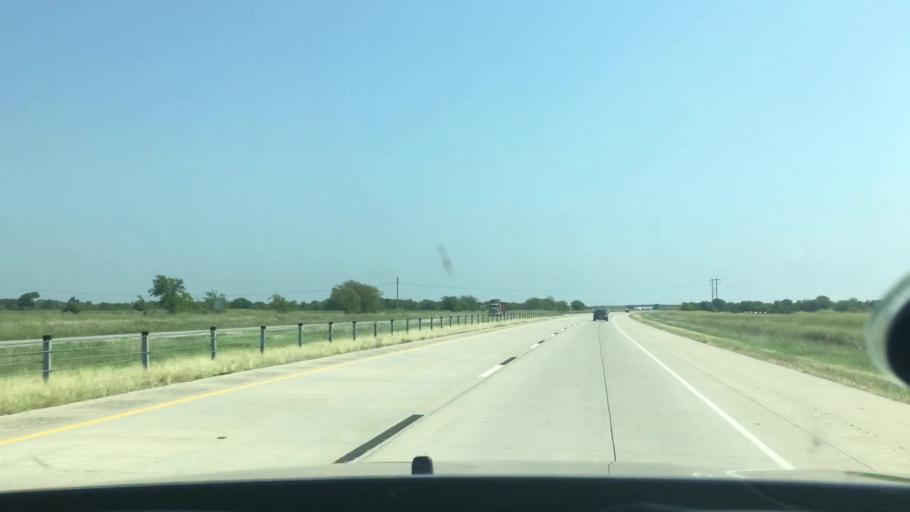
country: US
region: Oklahoma
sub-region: Bryan County
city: Durant
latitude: 34.0857
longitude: -96.3307
